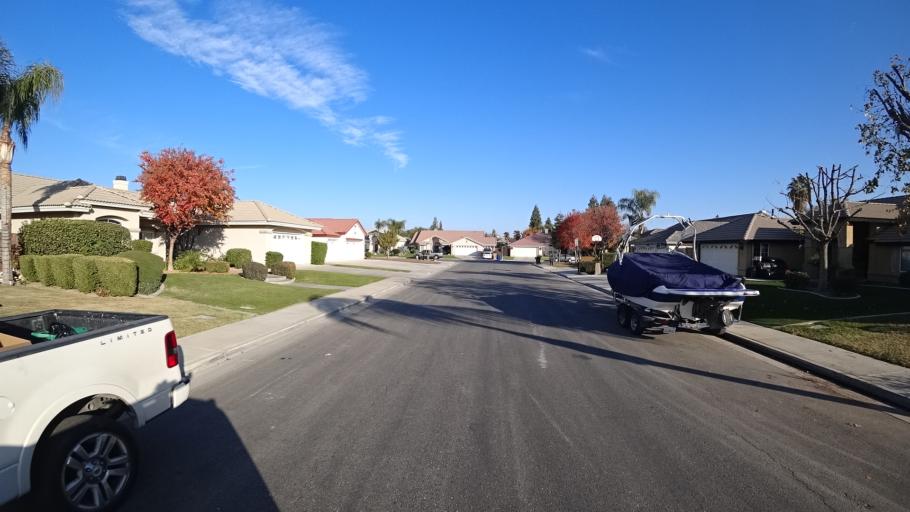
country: US
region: California
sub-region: Kern County
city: Greenfield
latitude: 35.2751
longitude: -119.0496
